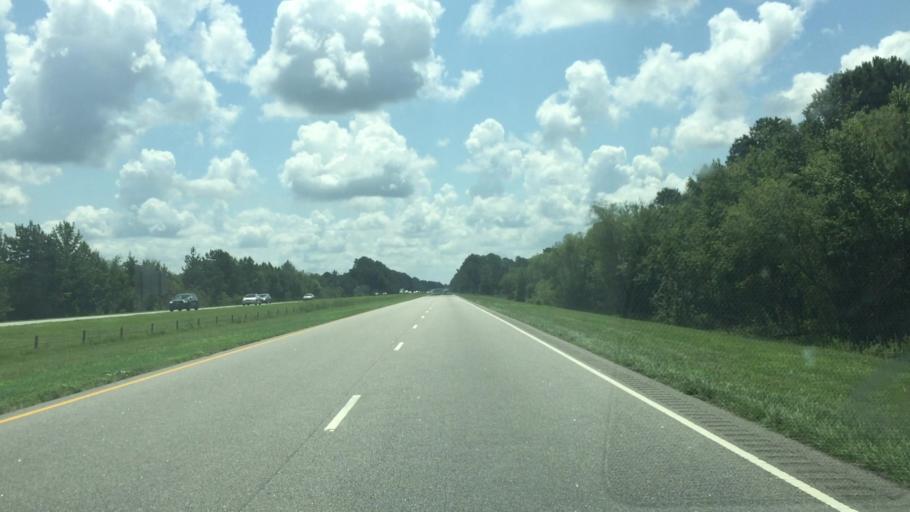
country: US
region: North Carolina
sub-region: Robeson County
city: Maxton
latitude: 34.7418
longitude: -79.3313
